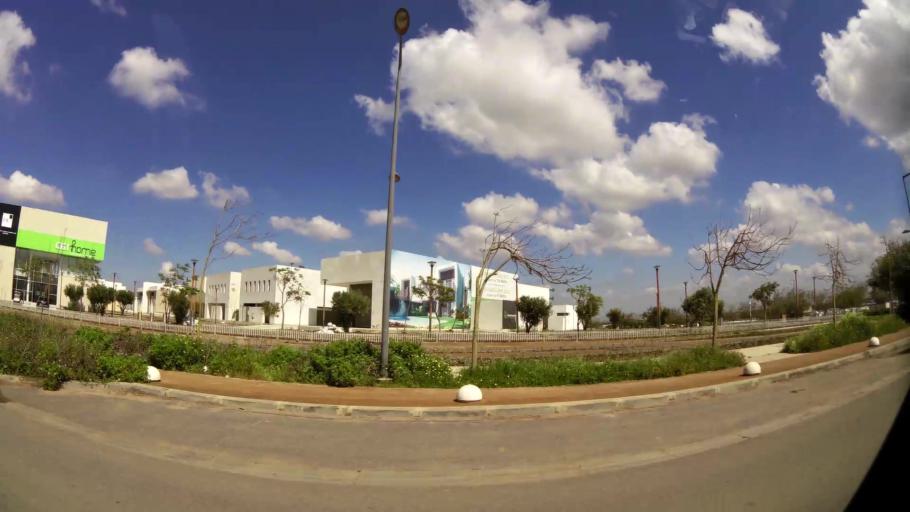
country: MA
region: Grand Casablanca
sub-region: Nouaceur
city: Bouskoura
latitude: 33.4939
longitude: -7.6036
